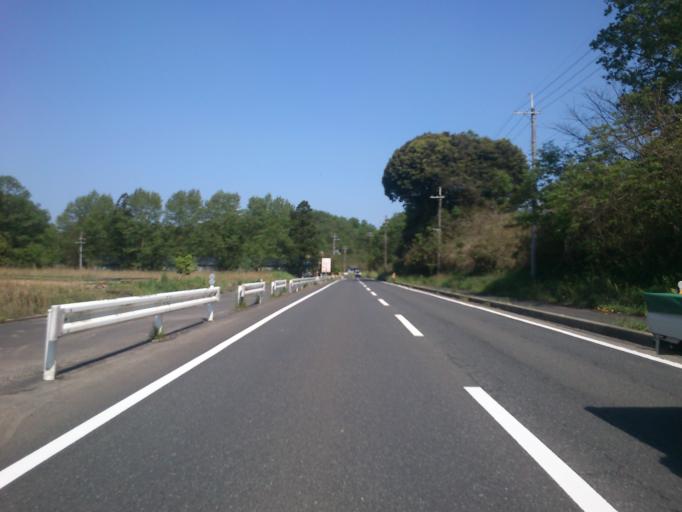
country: JP
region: Kyoto
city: Miyazu
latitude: 35.6787
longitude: 135.0698
